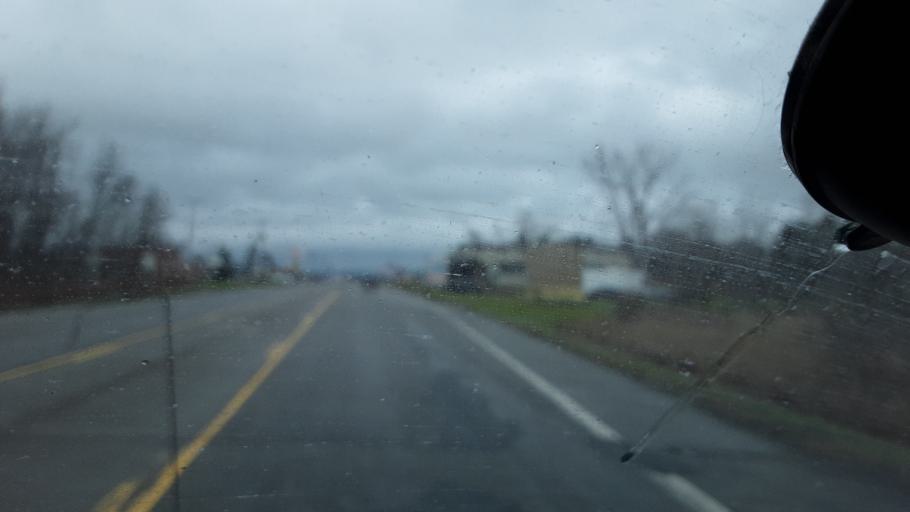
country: US
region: New York
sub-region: Cattaraugus County
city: Yorkshire
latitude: 42.5263
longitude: -78.4785
